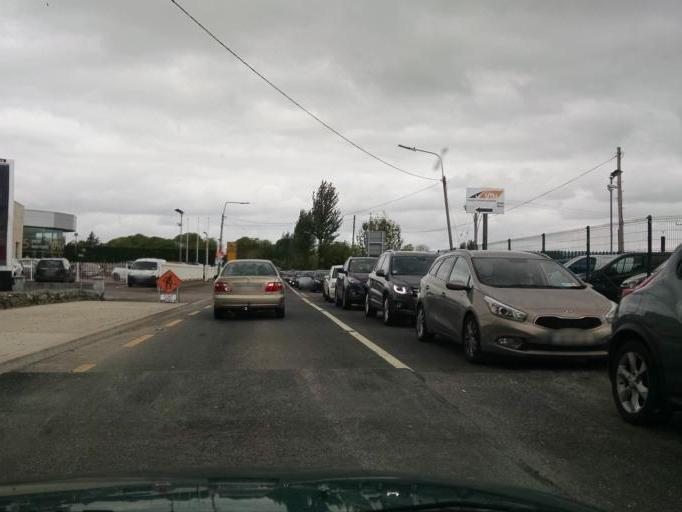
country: IE
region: Munster
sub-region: County Cork
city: Mallow
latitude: 52.2351
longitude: -8.6699
